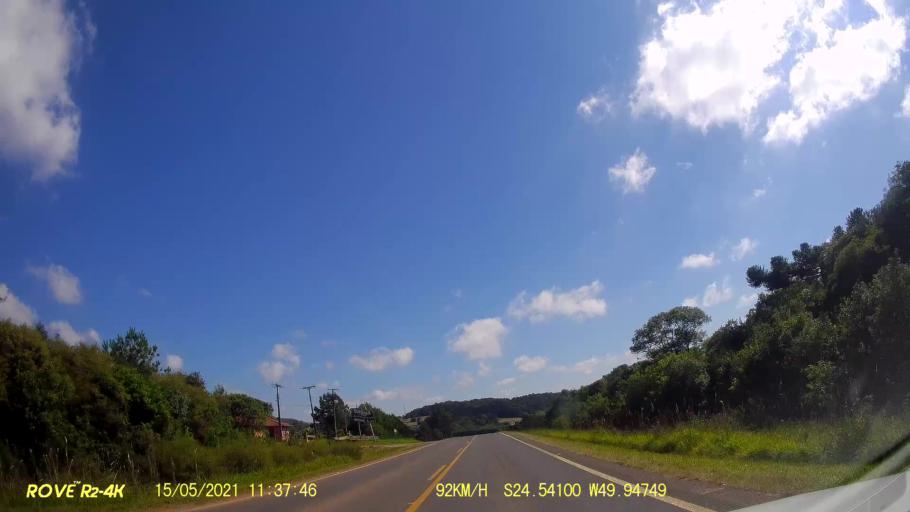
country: BR
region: Parana
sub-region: Pirai Do Sul
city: Pirai do Sul
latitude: -24.5411
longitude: -49.9472
